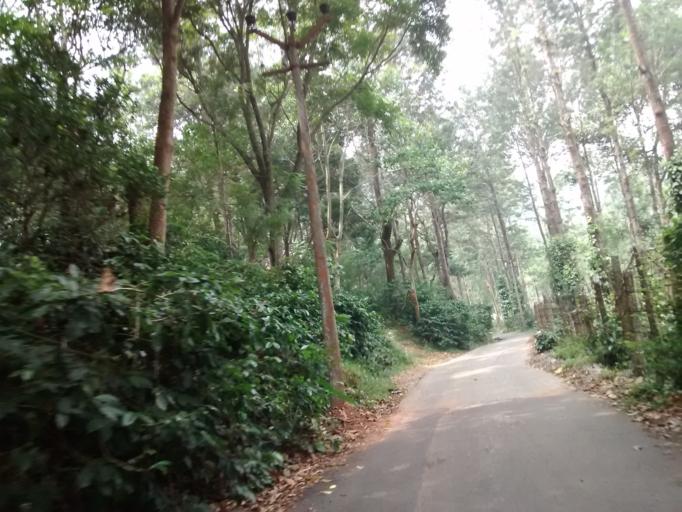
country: IN
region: Tamil Nadu
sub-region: Salem
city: Salem
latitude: 11.7891
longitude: 78.2037
